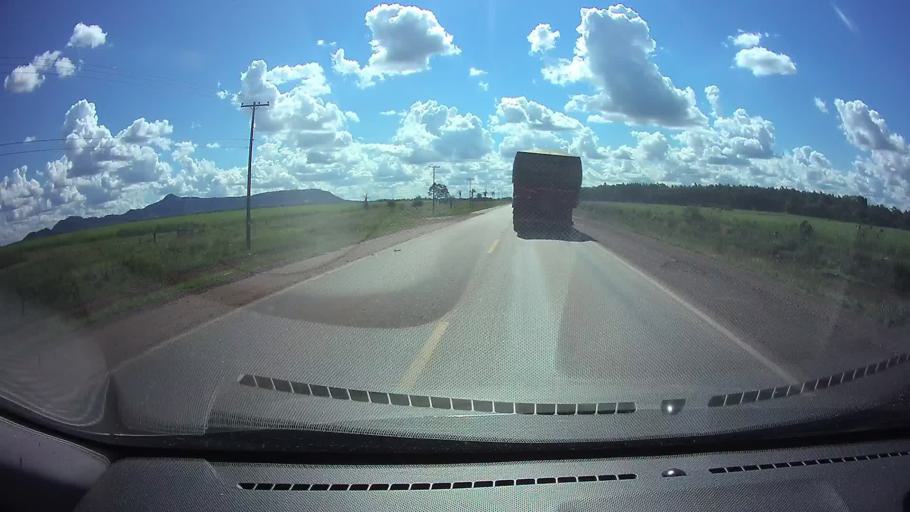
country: PY
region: Guaira
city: Coronel Martinez
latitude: -25.7620
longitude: -56.7396
